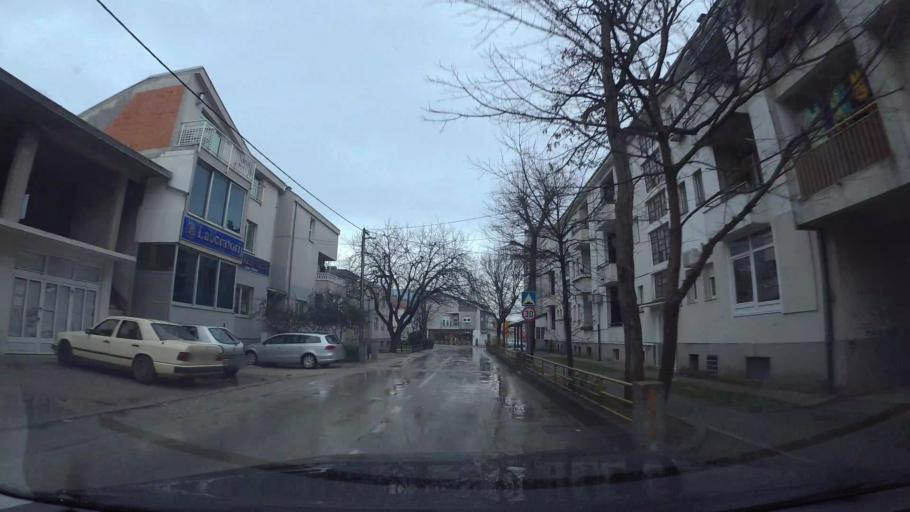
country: BA
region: Federation of Bosnia and Herzegovina
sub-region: Hercegovacko-Bosanski Kanton
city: Mostar
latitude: 43.3562
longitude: 17.8010
